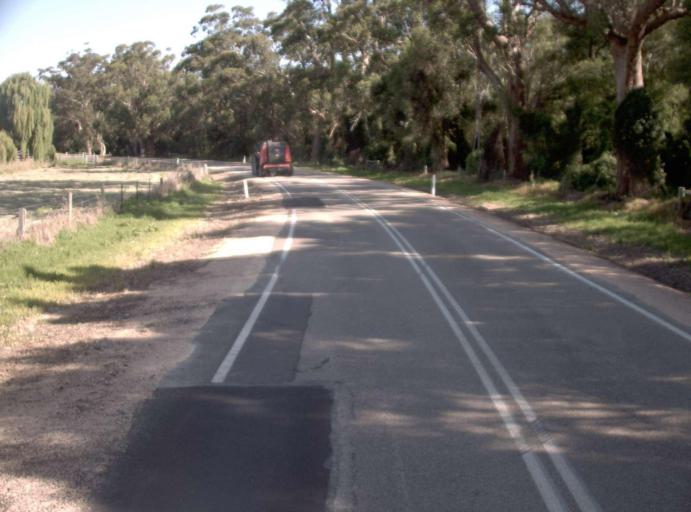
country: AU
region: Victoria
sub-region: East Gippsland
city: Lakes Entrance
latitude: -37.7379
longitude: 148.5050
